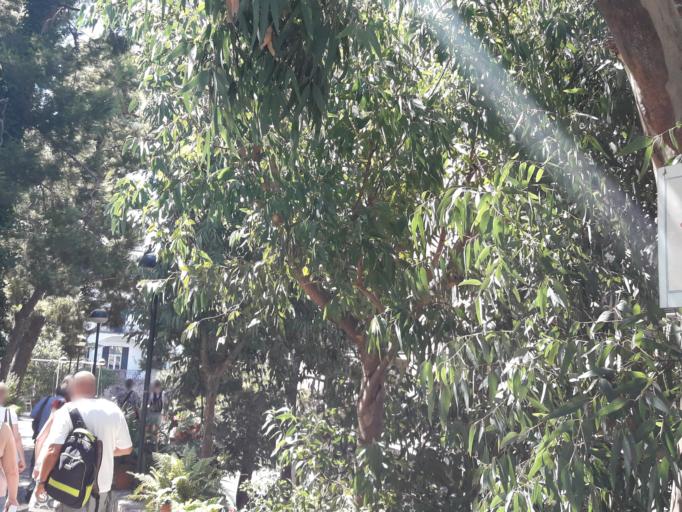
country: IT
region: Campania
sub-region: Provincia di Napoli
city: Sorrento
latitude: 40.6248
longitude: 14.3775
